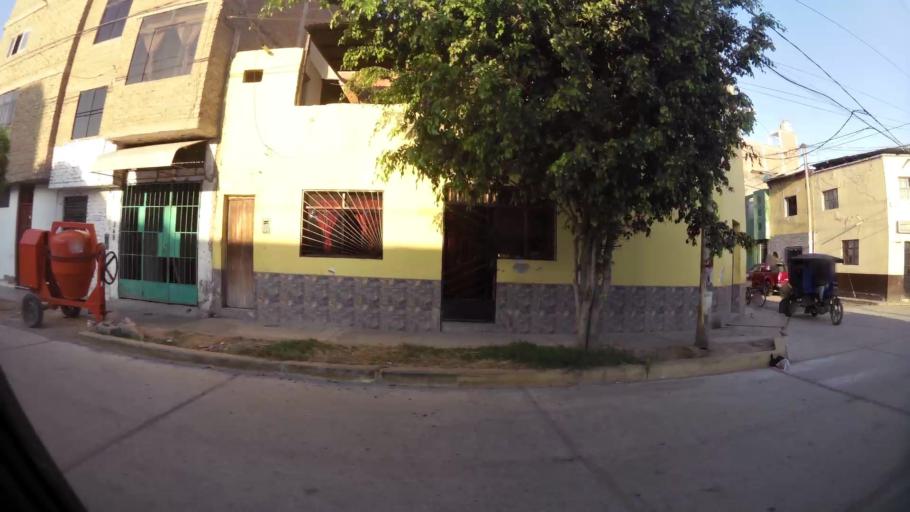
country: PE
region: Lambayeque
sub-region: Provincia de Chiclayo
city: Santa Rosa
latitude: -6.7716
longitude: -79.8295
